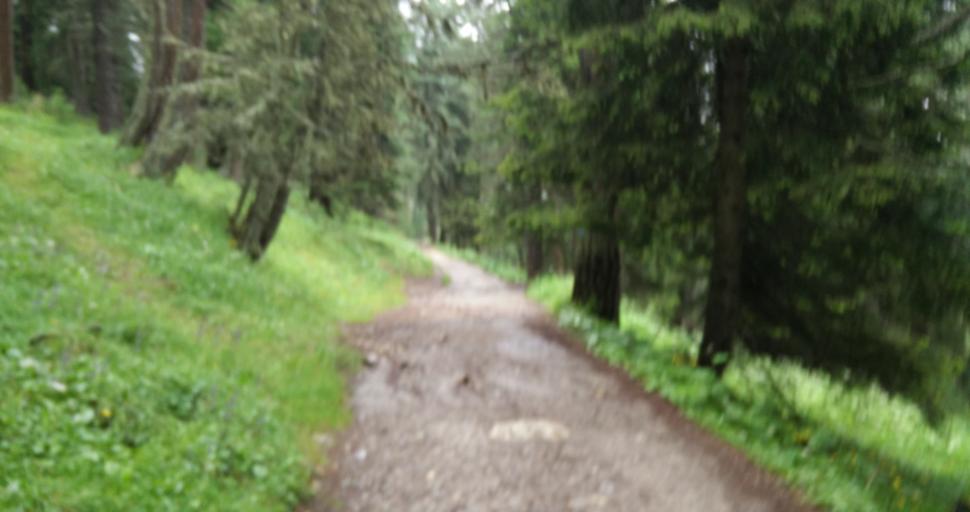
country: IT
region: Trentino-Alto Adige
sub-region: Provincia di Trento
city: Vigo di Fassa
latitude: 46.4347
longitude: 11.6586
